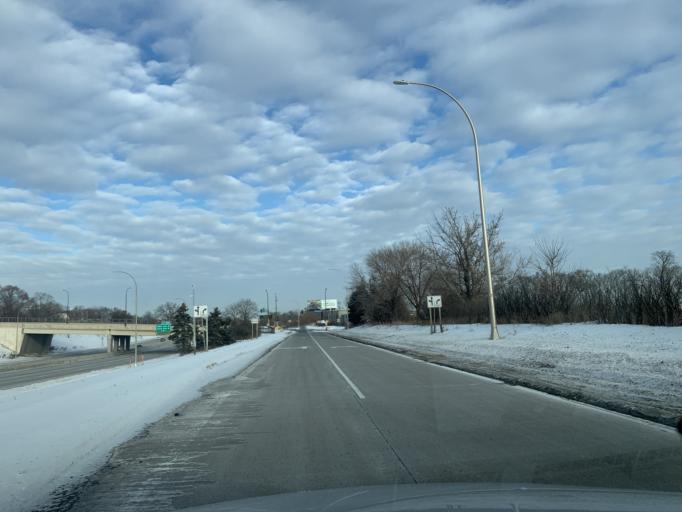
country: US
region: Minnesota
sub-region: Anoka County
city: Columbia Heights
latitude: 45.0226
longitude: -93.2832
